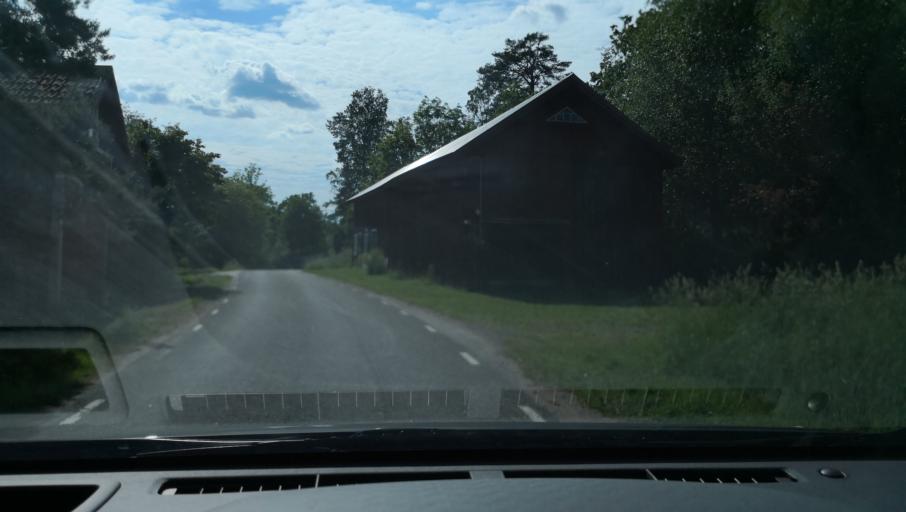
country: SE
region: Uppsala
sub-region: Enkopings Kommun
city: Orsundsbro
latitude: 59.8416
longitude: 17.1985
